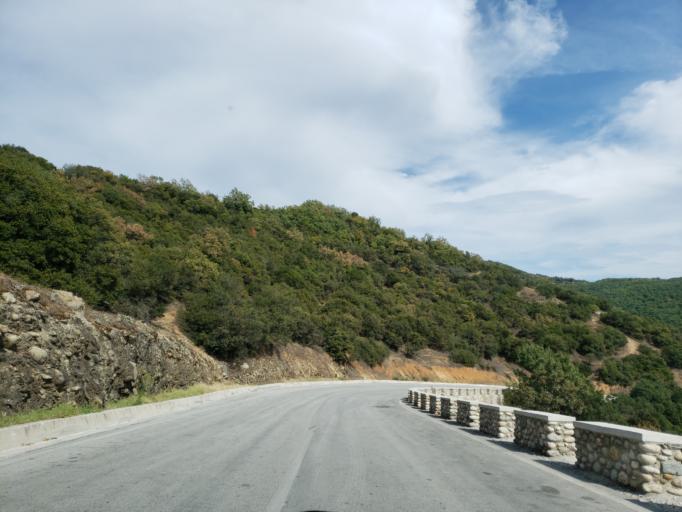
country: GR
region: Thessaly
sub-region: Trikala
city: Kastraki
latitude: 39.7264
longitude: 21.6308
